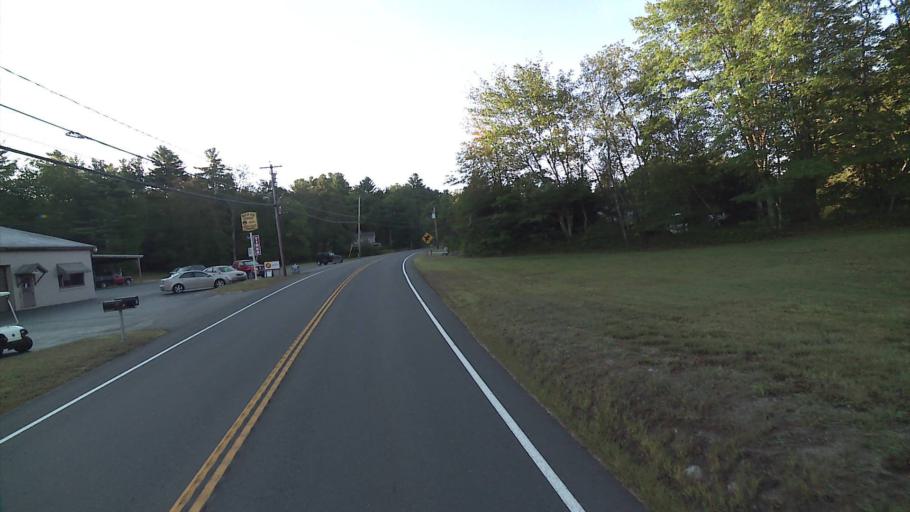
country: US
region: Connecticut
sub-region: Tolland County
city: Stafford
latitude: 41.9964
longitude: -72.3159
